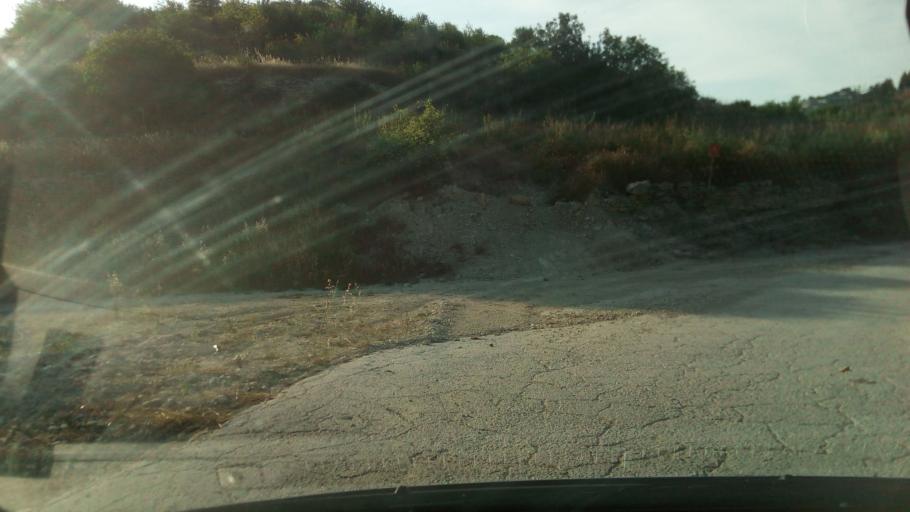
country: CY
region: Pafos
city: Tala
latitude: 34.8766
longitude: 32.4804
